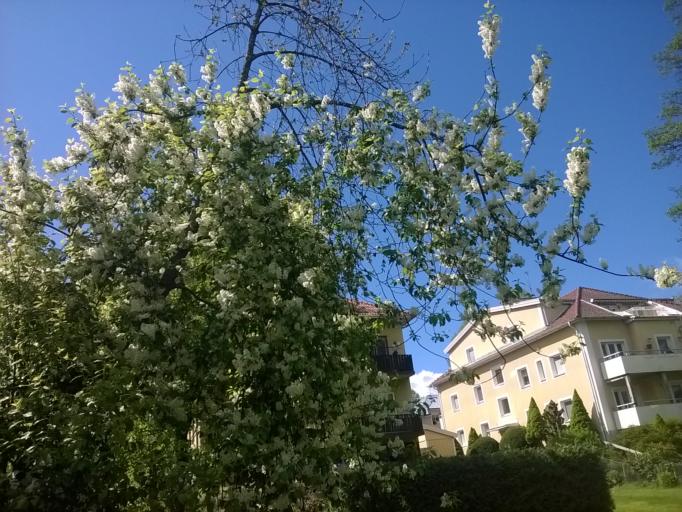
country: SE
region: OEstergoetland
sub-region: Norrkopings Kommun
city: Norrkoping
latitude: 58.5870
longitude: 16.1609
